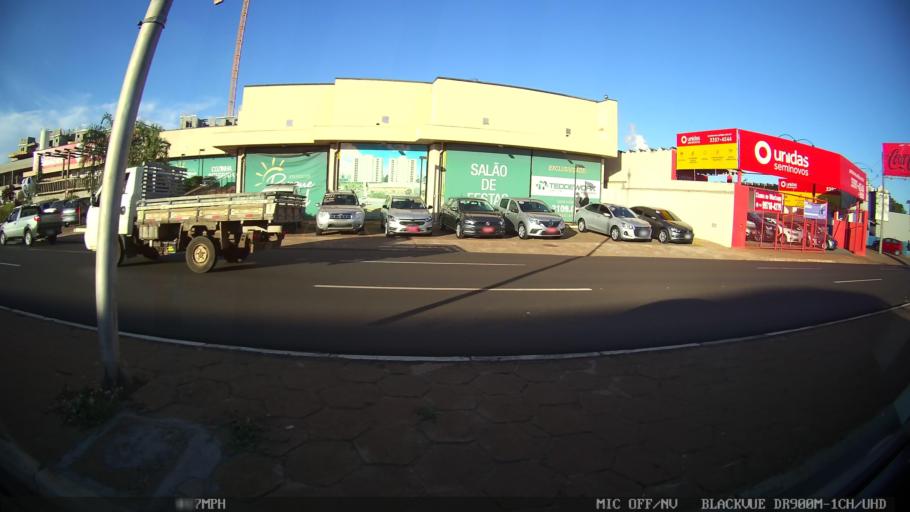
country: BR
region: Sao Paulo
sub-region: Araraquara
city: Araraquara
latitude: -21.8025
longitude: -48.1730
